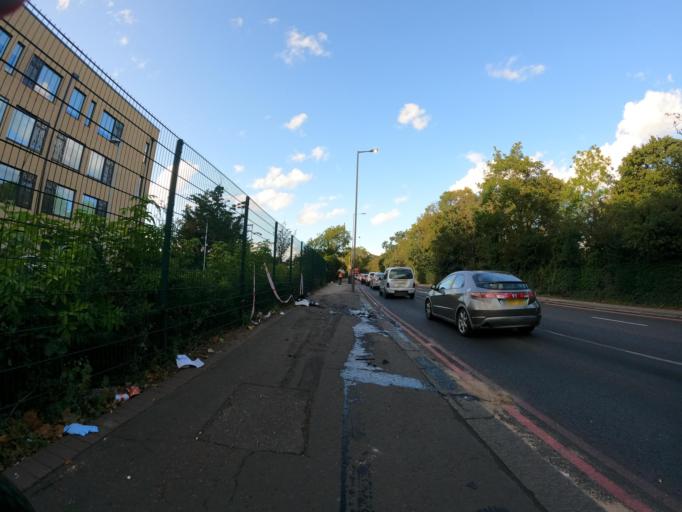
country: GB
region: England
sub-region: Greater London
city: Ealing Broadway
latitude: 51.5194
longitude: -0.2915
